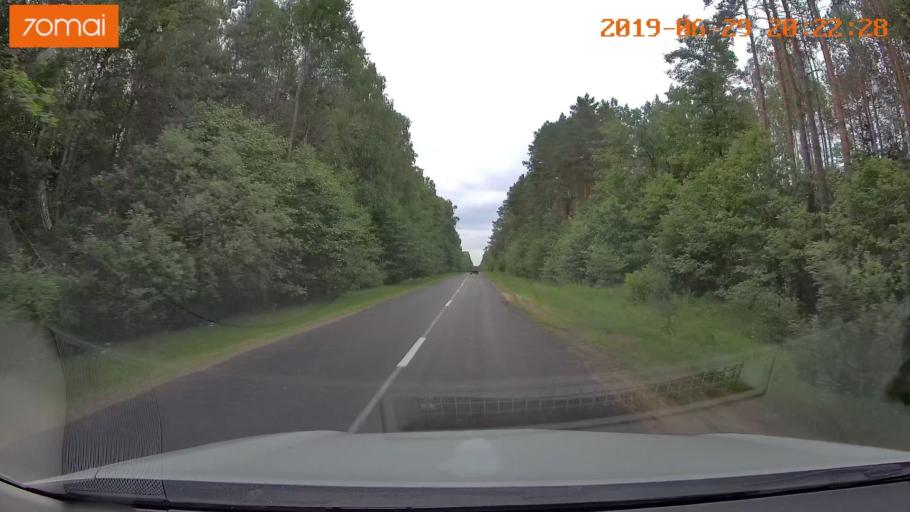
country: BY
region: Brest
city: Asnyezhytsy
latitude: 52.4325
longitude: 26.2549
